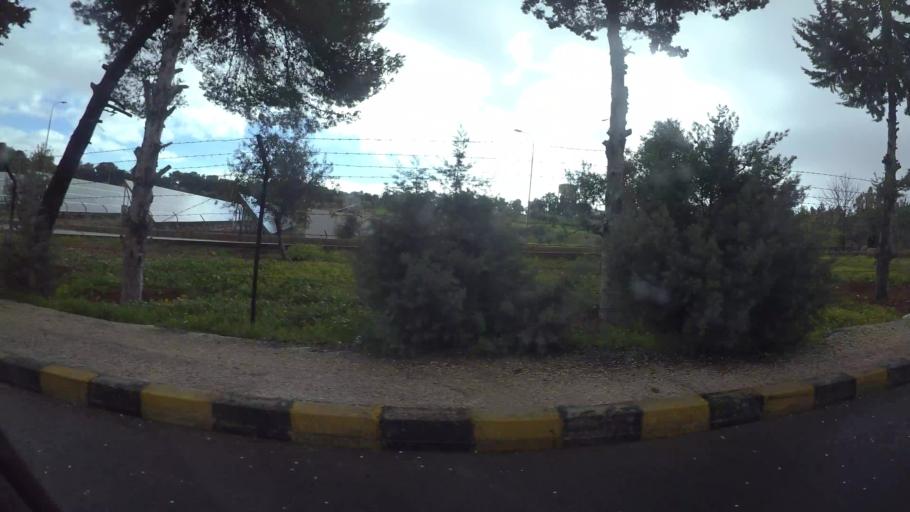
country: JO
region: Amman
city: Al Jubayhah
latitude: 32.0272
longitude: 35.8778
